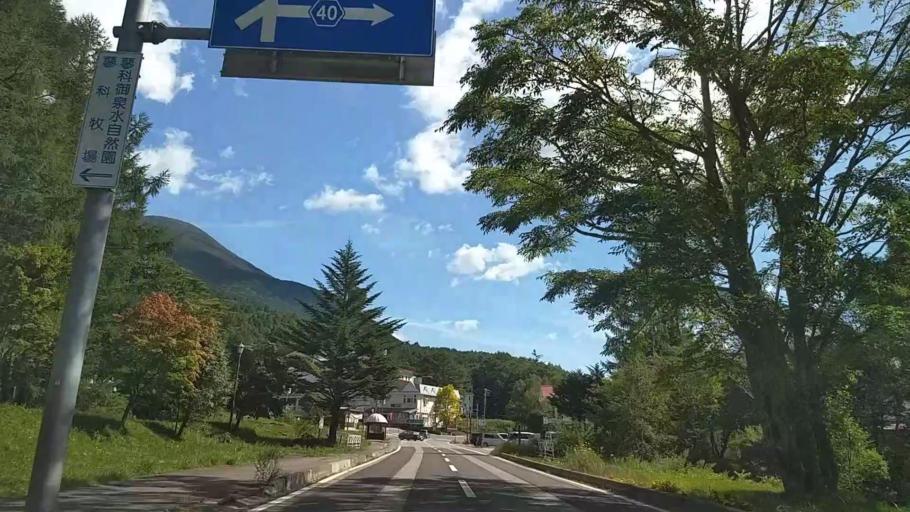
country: JP
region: Nagano
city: Chino
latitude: 36.1304
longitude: 138.2715
